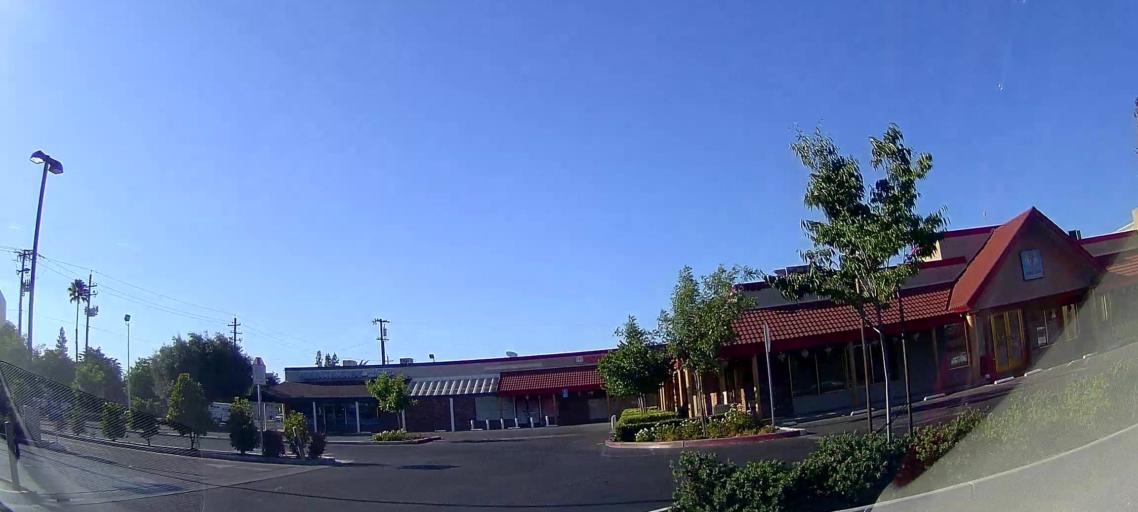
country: US
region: California
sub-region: Fresno County
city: Fresno
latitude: 36.8233
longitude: -119.8077
